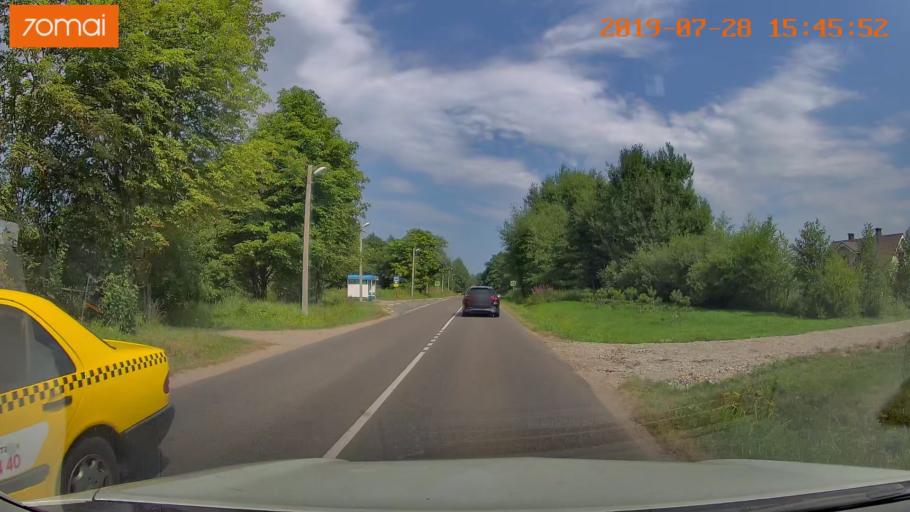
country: RU
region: Kaliningrad
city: Otradnoye
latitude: 54.9423
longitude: 20.0464
